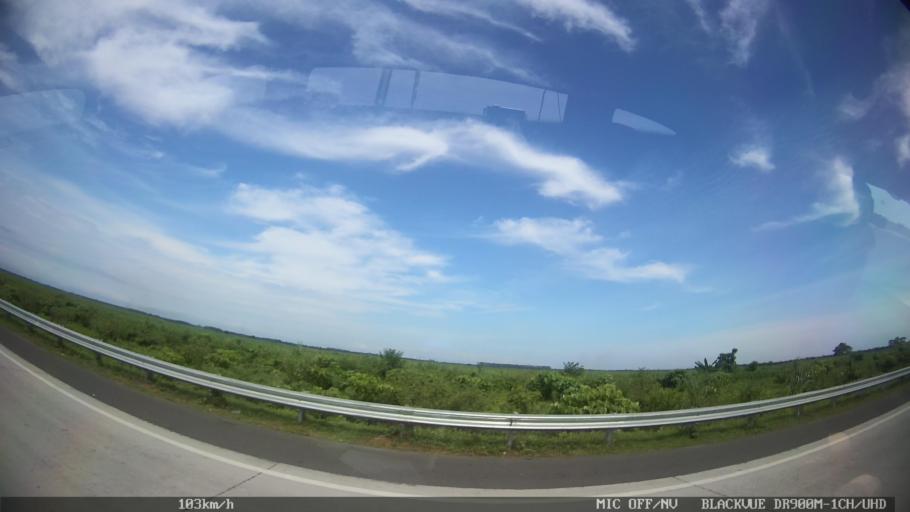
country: ID
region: North Sumatra
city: Binjai
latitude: 3.6787
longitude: 98.5366
